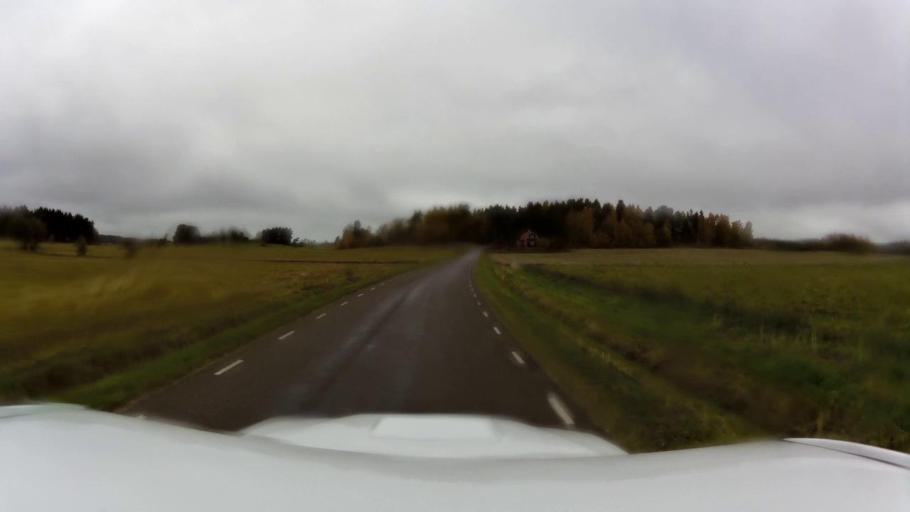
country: SE
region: OEstergoetland
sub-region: Linkopings Kommun
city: Linghem
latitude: 58.4612
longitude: 15.8280
